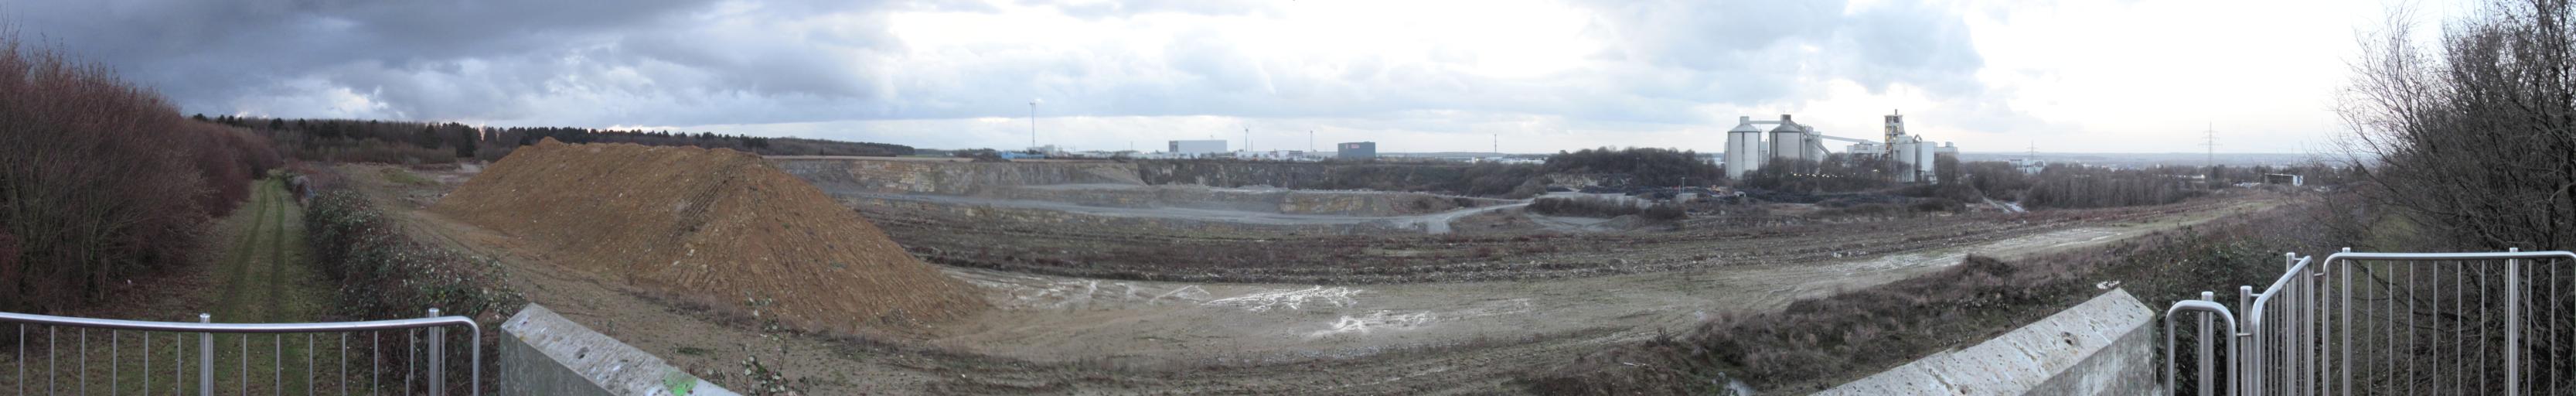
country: DE
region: North Rhine-Westphalia
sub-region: Regierungsbezirk Detmold
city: Paderborn
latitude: 51.6982
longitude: 8.7557
